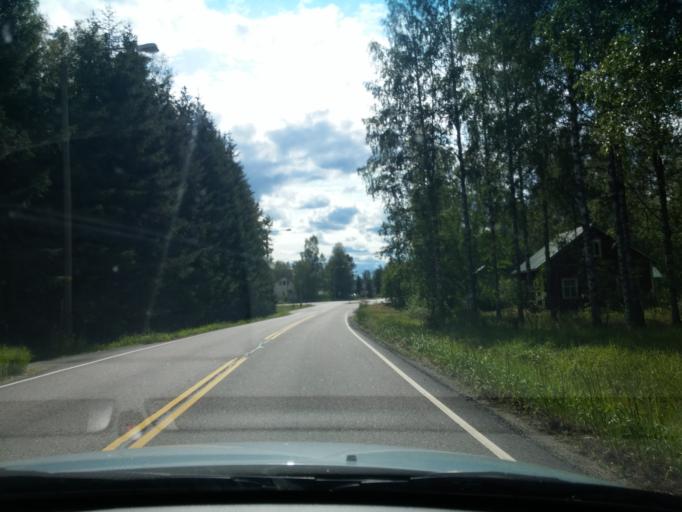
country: FI
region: Central Finland
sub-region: Saarijaervi-Viitasaari
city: Pylkoenmaeki
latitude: 62.5900
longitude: 24.5954
